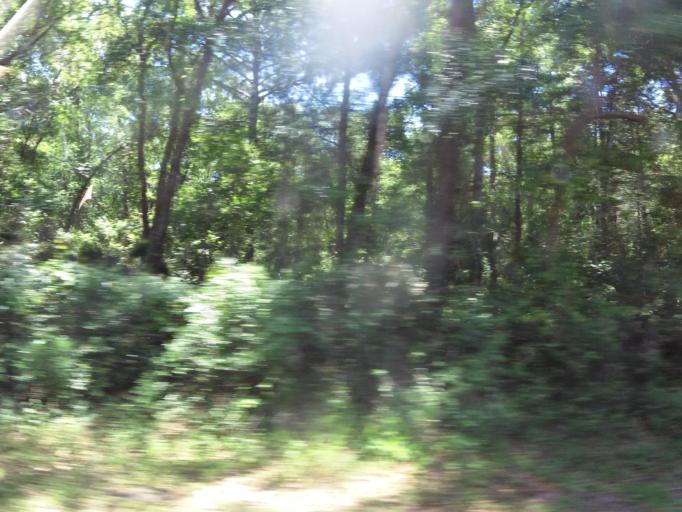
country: US
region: Florida
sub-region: Duval County
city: Atlantic Beach
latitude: 30.4581
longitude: -81.5202
